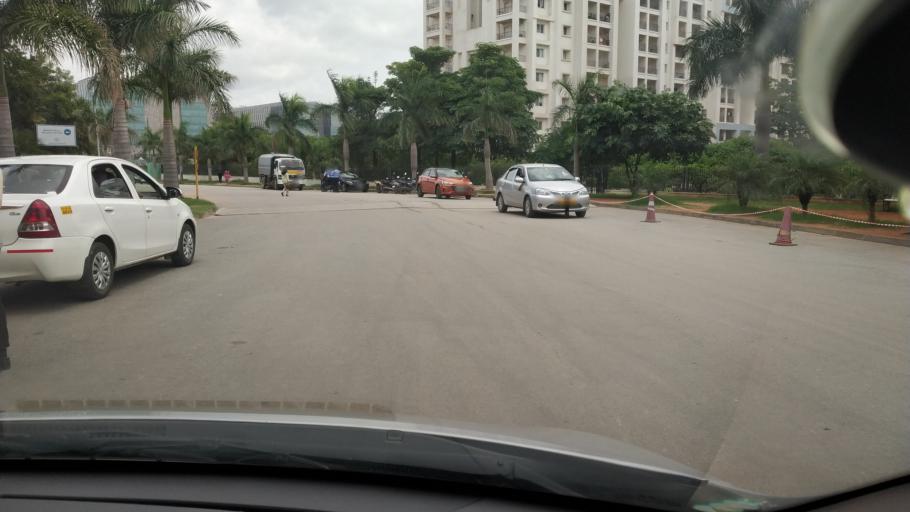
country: IN
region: Karnataka
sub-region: Bangalore Urban
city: Bangalore
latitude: 12.9198
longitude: 77.6889
